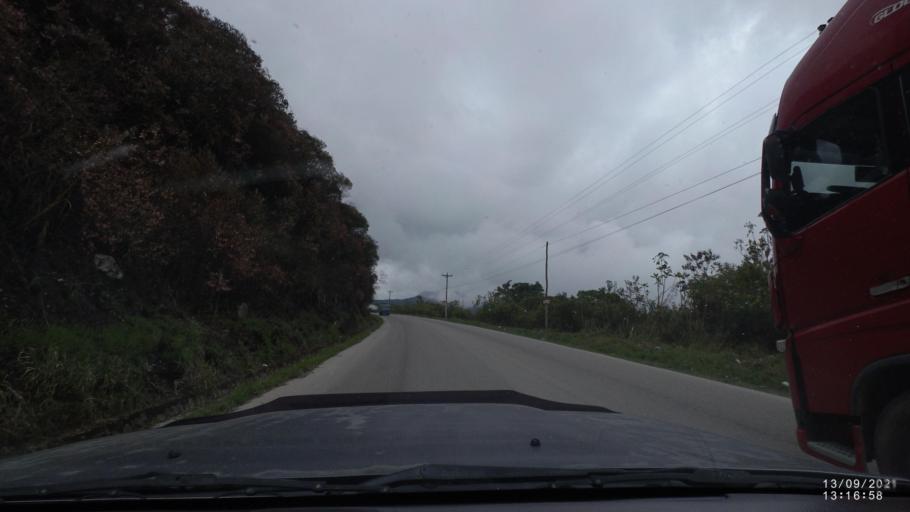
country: BO
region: Cochabamba
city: Colomi
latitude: -17.2012
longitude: -65.8607
